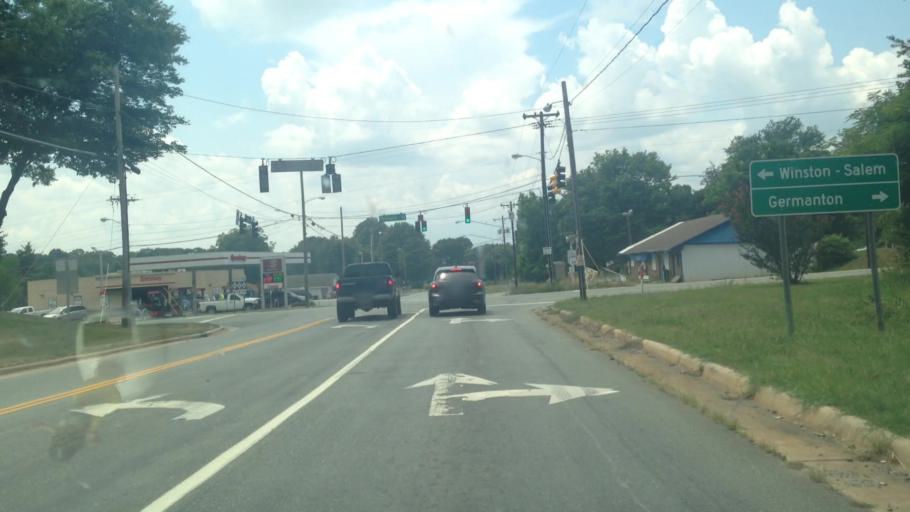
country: US
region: North Carolina
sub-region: Forsyth County
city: Rural Hall
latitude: 36.1948
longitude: -80.2540
